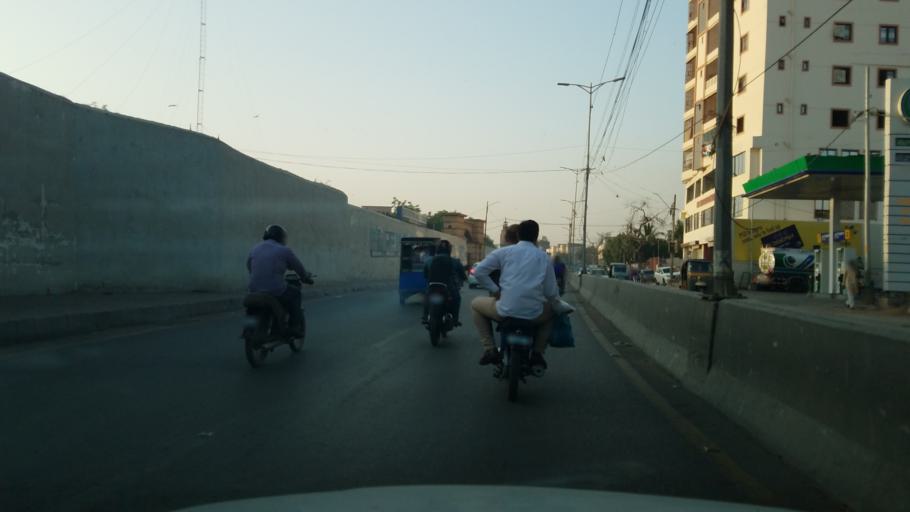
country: PK
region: Sindh
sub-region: Karachi District
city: Karachi
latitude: 24.8687
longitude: 67.0229
